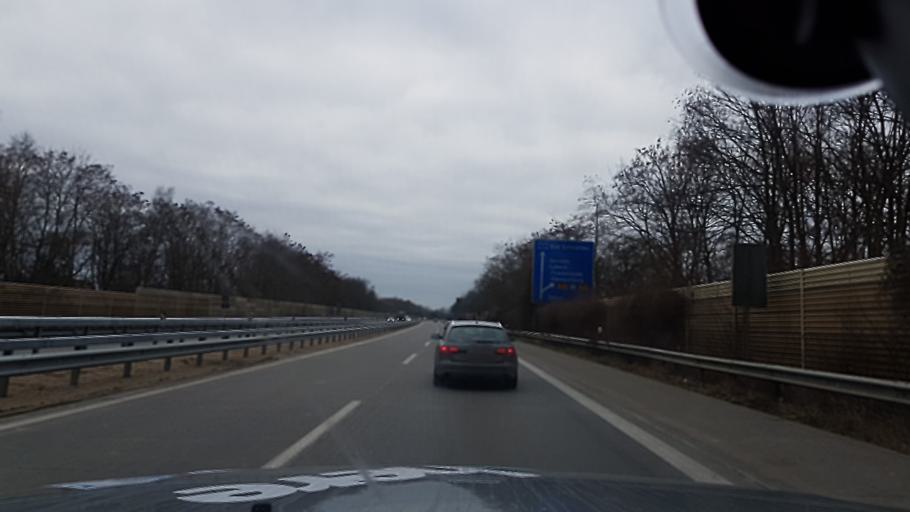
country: DE
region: Schleswig-Holstein
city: Ratekau
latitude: 53.9262
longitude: 10.7264
